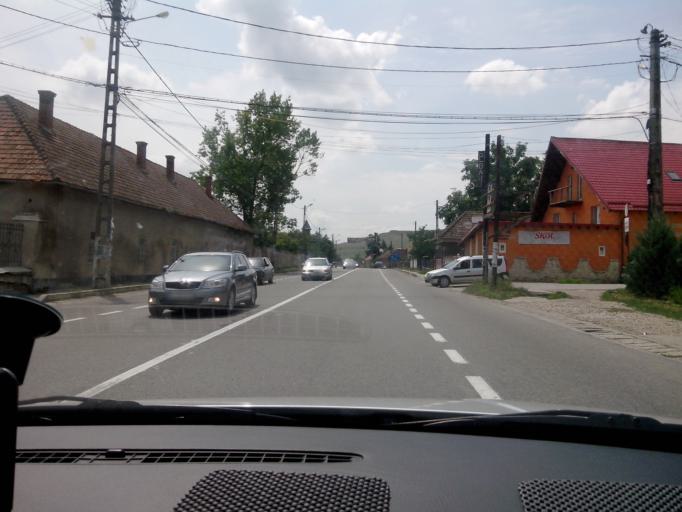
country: RO
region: Cluj
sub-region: Comuna Bontida
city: Rascruci
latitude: 46.9068
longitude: 23.7734
